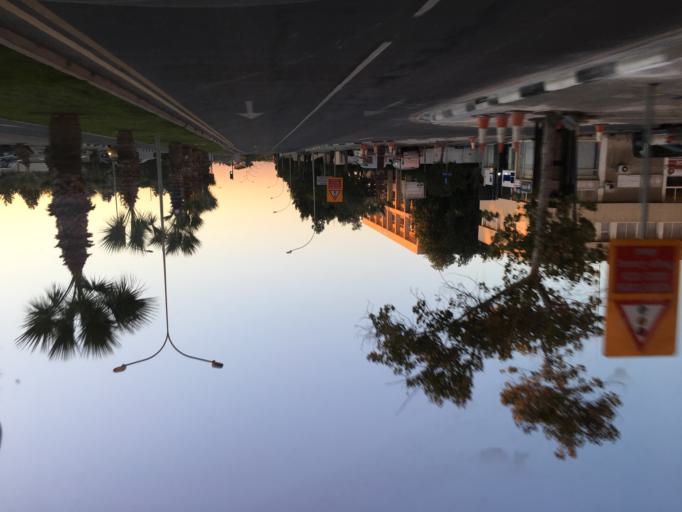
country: CY
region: Larnaka
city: Larnaca
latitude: 34.9018
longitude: 33.6304
